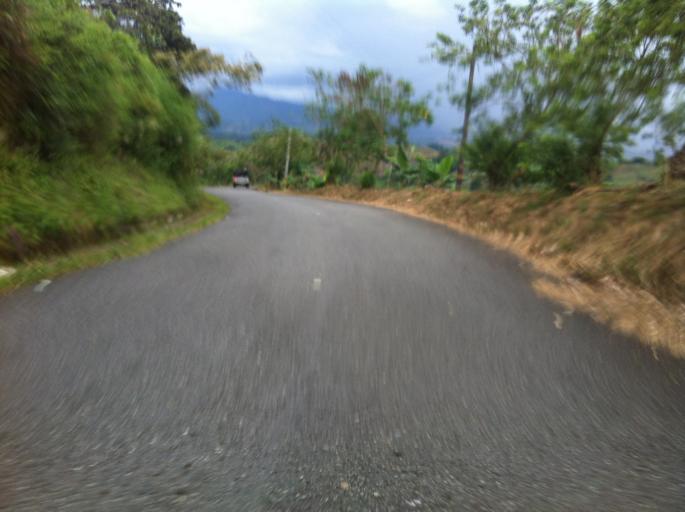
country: CO
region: Quindio
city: Buenavista
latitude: 4.3689
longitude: -75.7571
